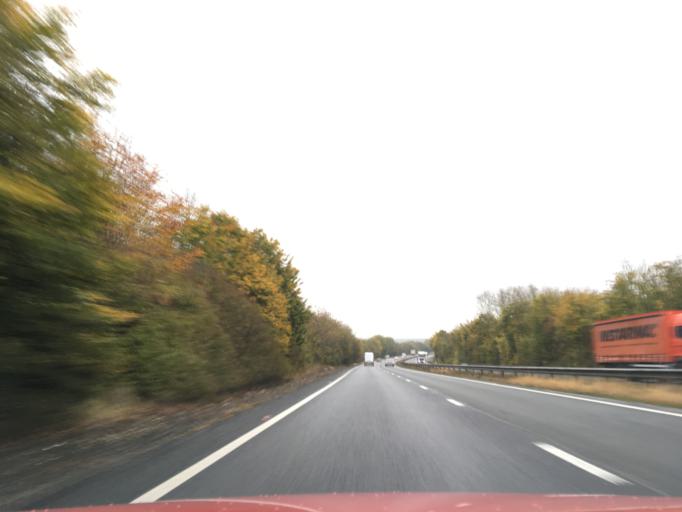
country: GB
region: England
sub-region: Hampshire
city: Highclere
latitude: 51.3250
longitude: -1.3442
